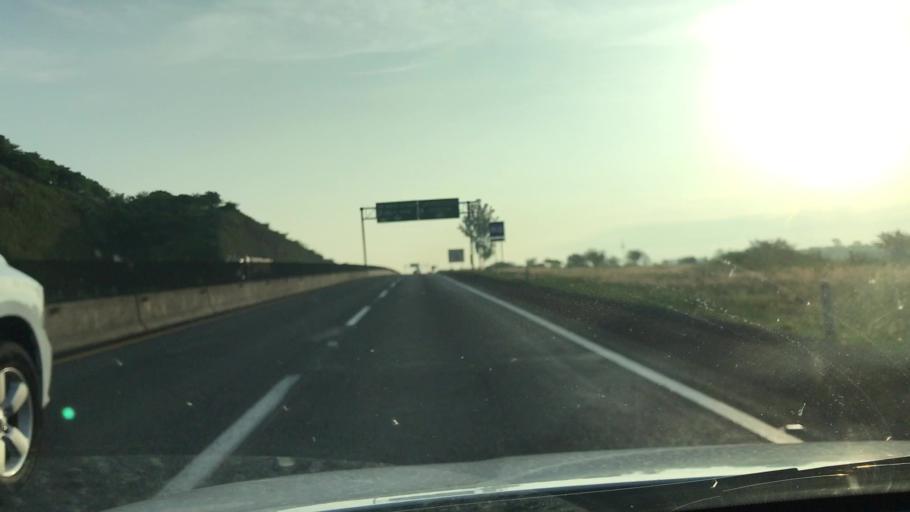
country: MX
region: Jalisco
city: Jalostotitlan
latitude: 21.1104
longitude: -102.4653
